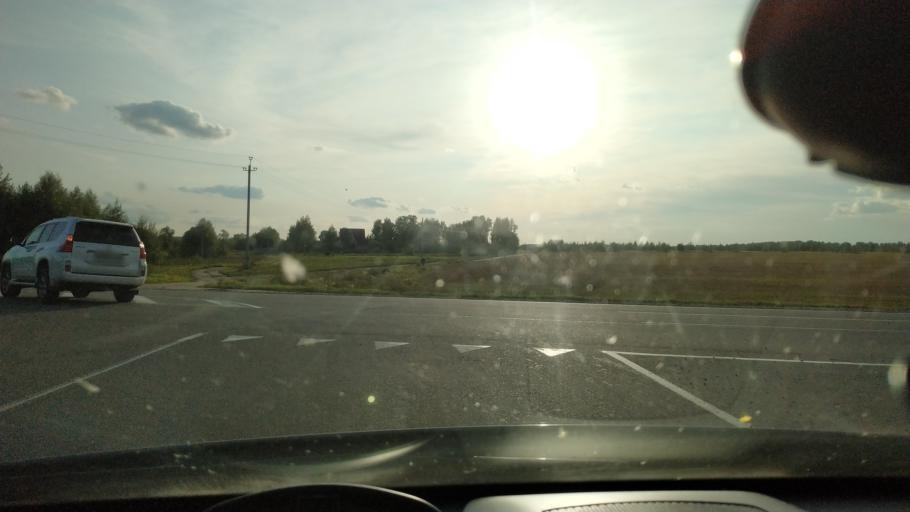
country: RU
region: Rjazan
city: Rybnoye
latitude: 54.8196
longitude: 39.6074
